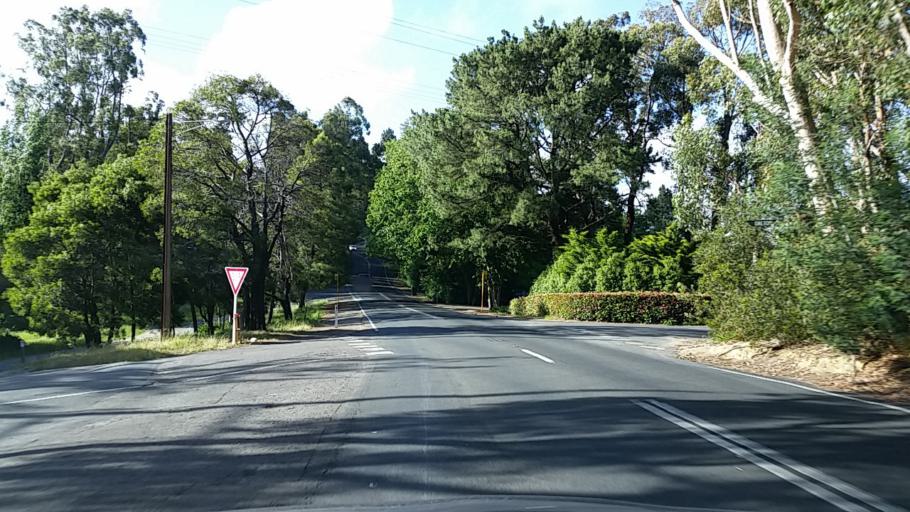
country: AU
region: South Australia
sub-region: Adelaide Hills
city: Stirling
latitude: -35.0241
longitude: 138.7550
